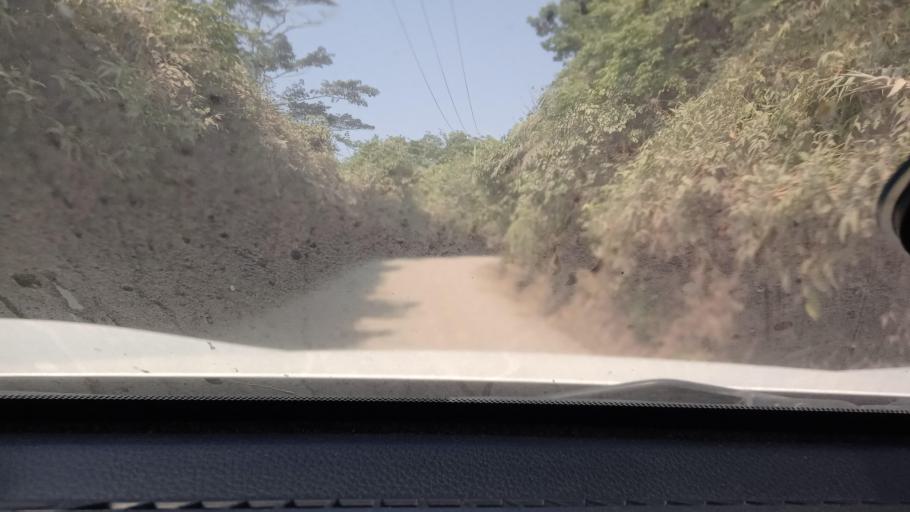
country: MX
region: Tabasco
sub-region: Huimanguillo
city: Francisco Rueda
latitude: 17.6532
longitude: -93.8841
